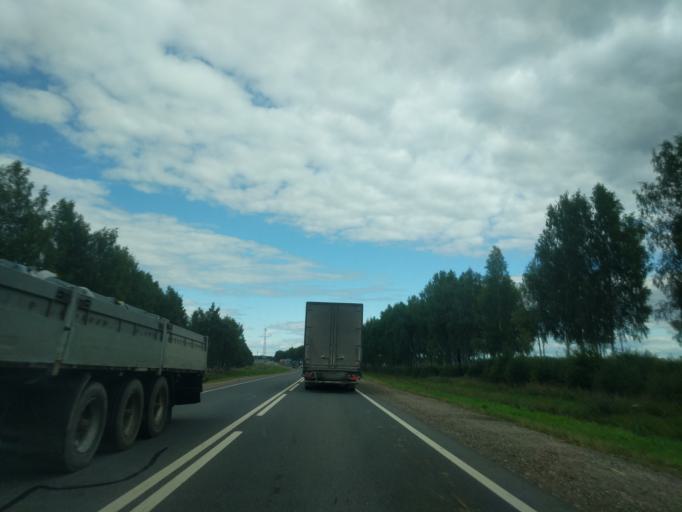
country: RU
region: Kostroma
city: Ostrovskoye
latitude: 57.8145
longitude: 42.2195
